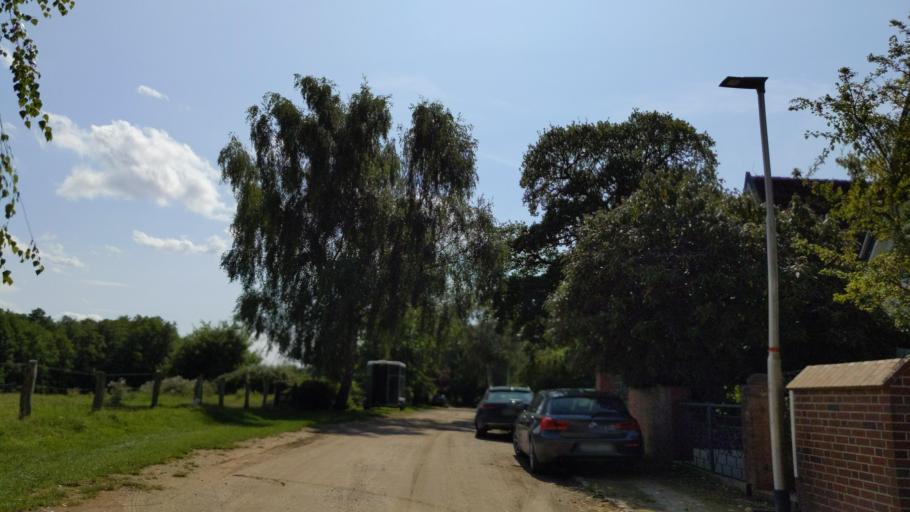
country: DE
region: Schleswig-Holstein
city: Bosdorf
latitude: 54.1696
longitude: 10.4896
